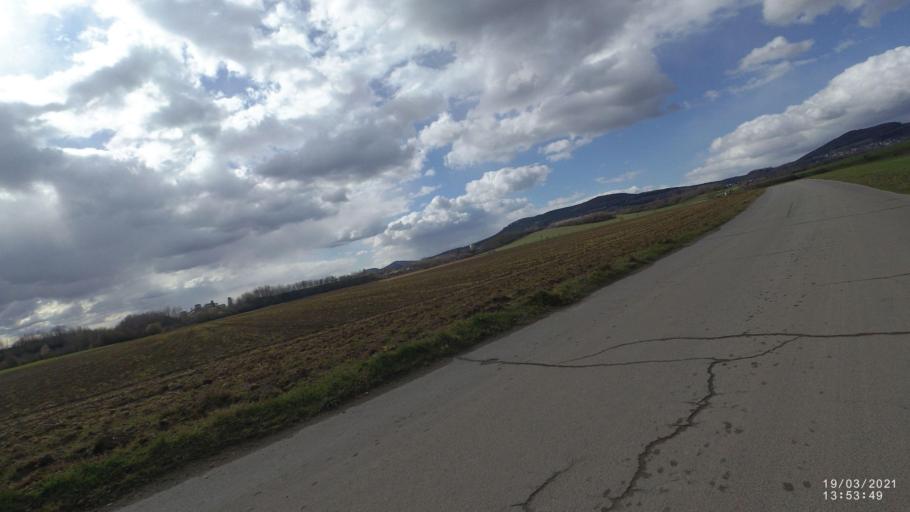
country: DE
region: Rheinland-Pfalz
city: Kretz
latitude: 50.4015
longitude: 7.3570
